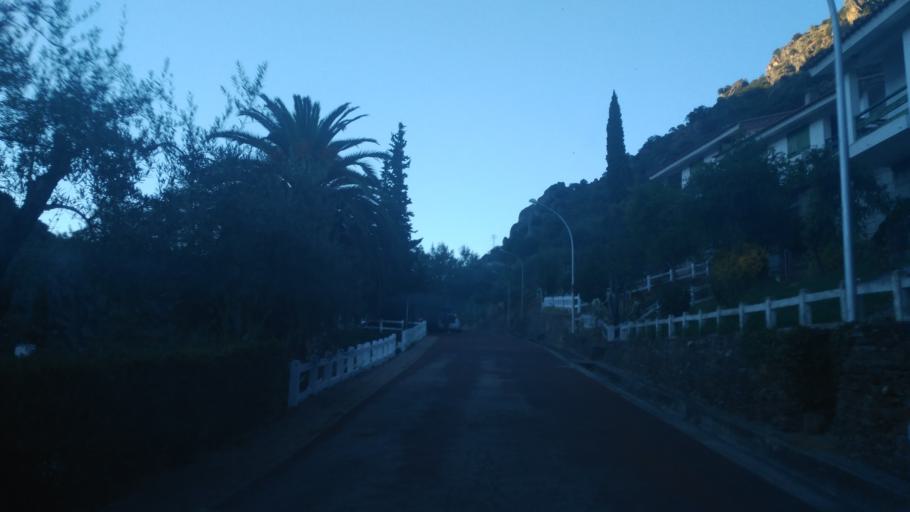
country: ES
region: Castille and Leon
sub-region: Provincia de Salamanca
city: Mieza
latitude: 41.1938
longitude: -6.6886
